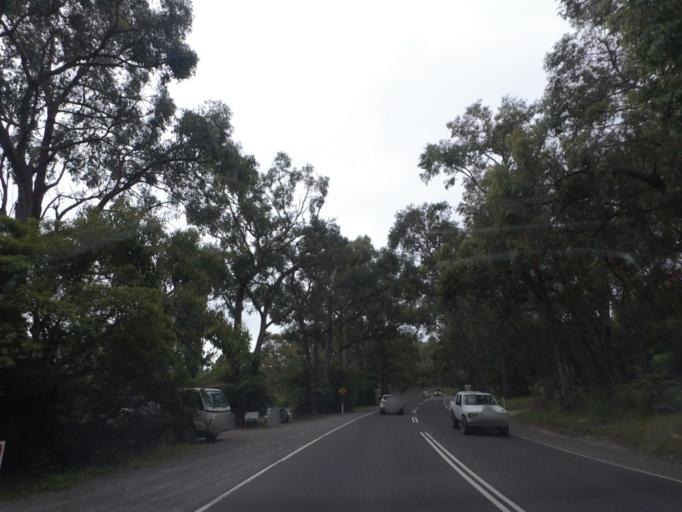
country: AU
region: Victoria
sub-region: Yarra Ranges
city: Mount Evelyn
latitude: -37.7923
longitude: 145.3756
